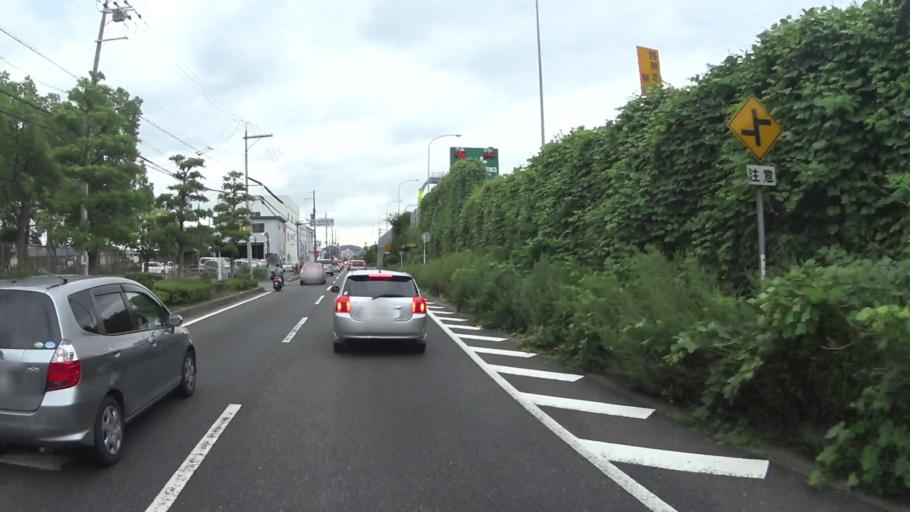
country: JP
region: Kyoto
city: Muko
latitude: 34.9228
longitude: 135.7107
